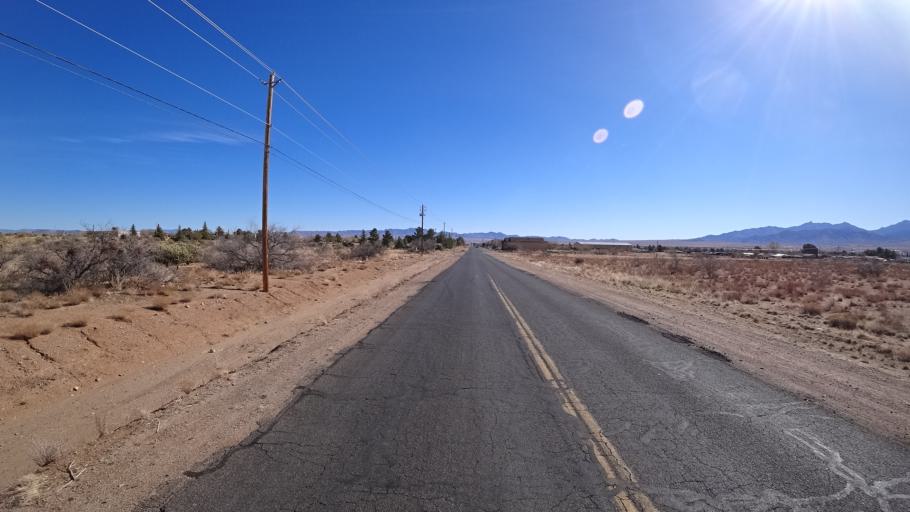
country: US
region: Arizona
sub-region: Mohave County
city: New Kingman-Butler
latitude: 35.2685
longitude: -114.0338
